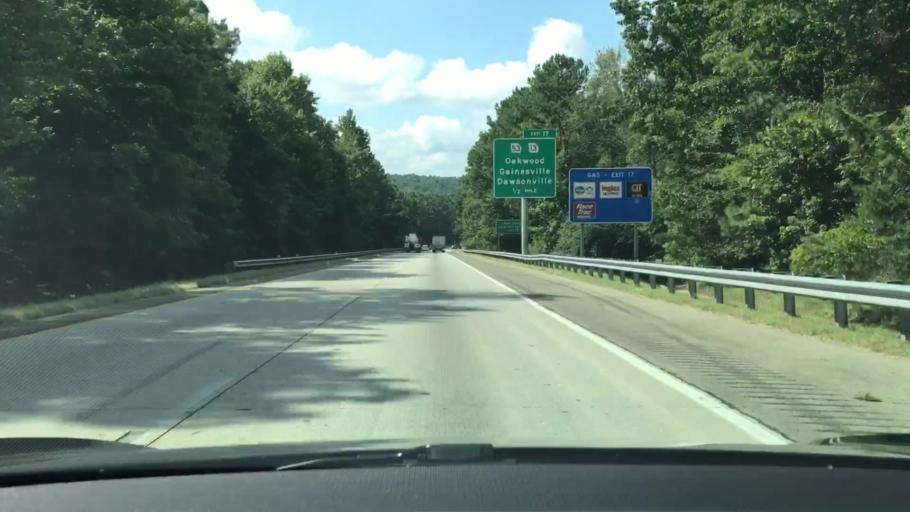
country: US
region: Georgia
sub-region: Hall County
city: Oakwood
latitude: 34.2405
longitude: -83.8407
